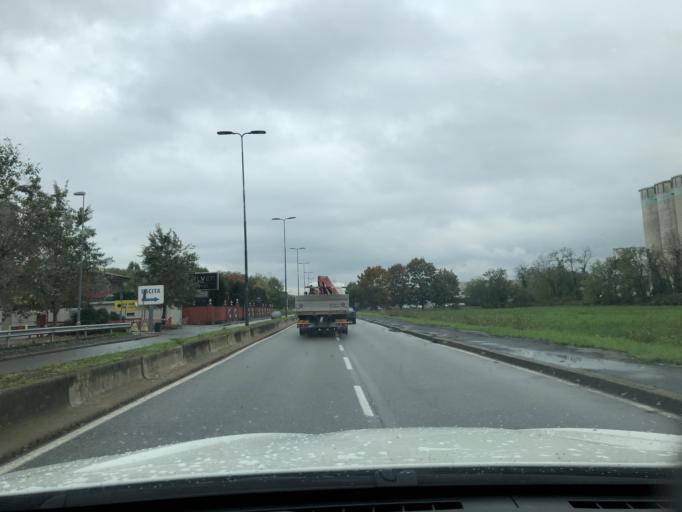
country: IT
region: Lombardy
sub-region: Citta metropolitana di Milano
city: Settimo Milanese
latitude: 45.4584
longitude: 9.0695
